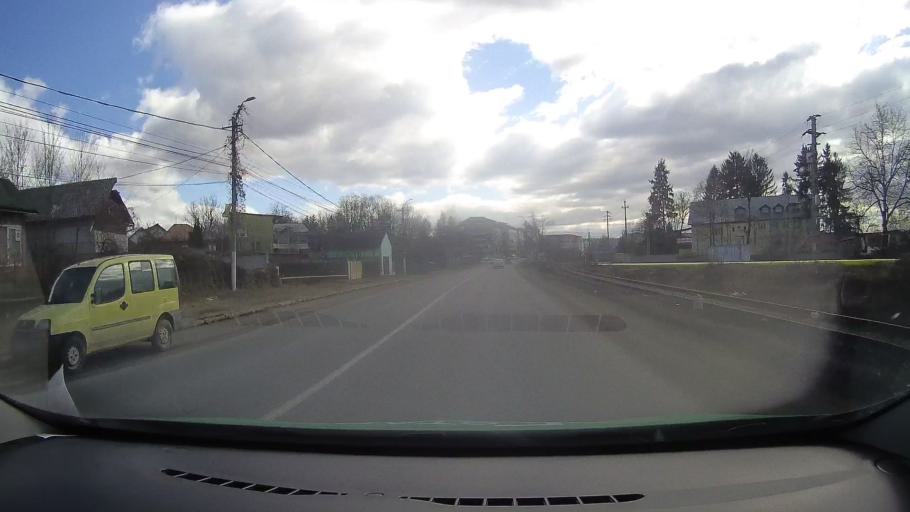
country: RO
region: Dambovita
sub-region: Oras Pucioasa
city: Pucioasa
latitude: 45.0807
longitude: 25.4264
